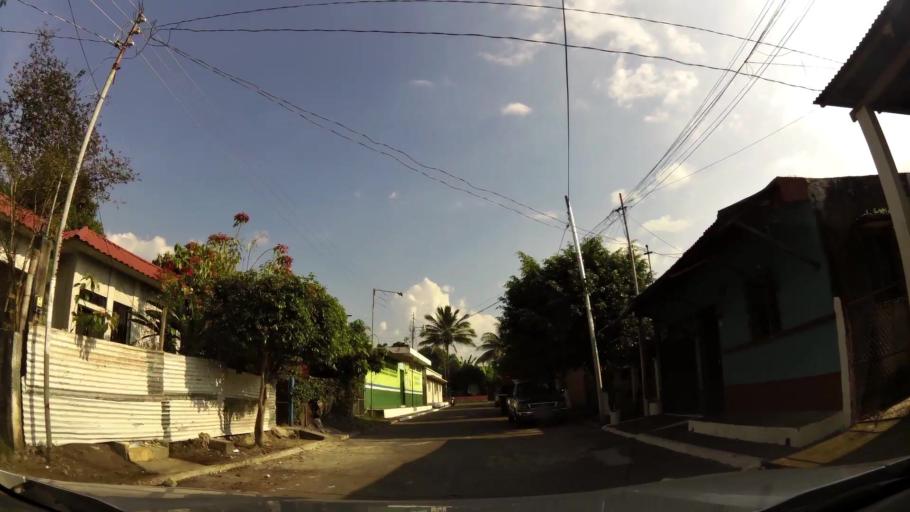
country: GT
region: Retalhuleu
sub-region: Municipio de Retalhuleu
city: Retalhuleu
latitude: 14.5287
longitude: -91.6897
